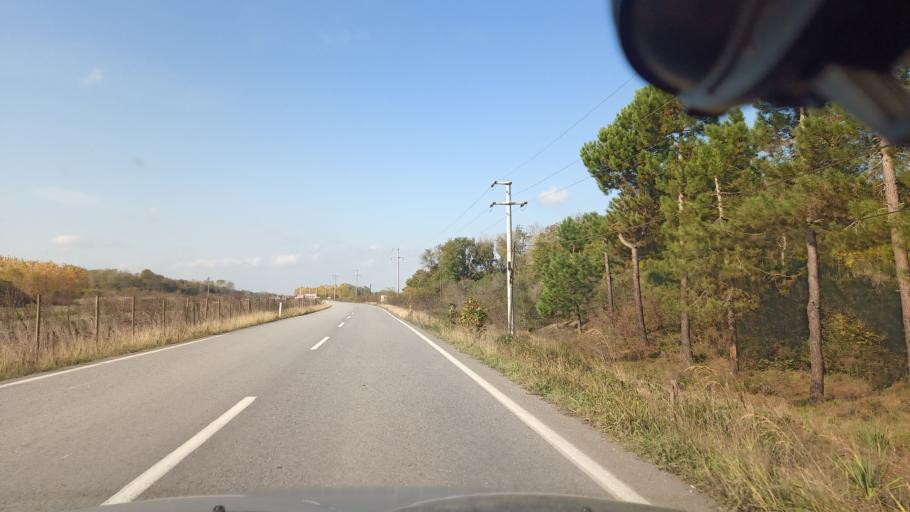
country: TR
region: Sakarya
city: Karasu
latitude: 41.1201
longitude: 30.5998
